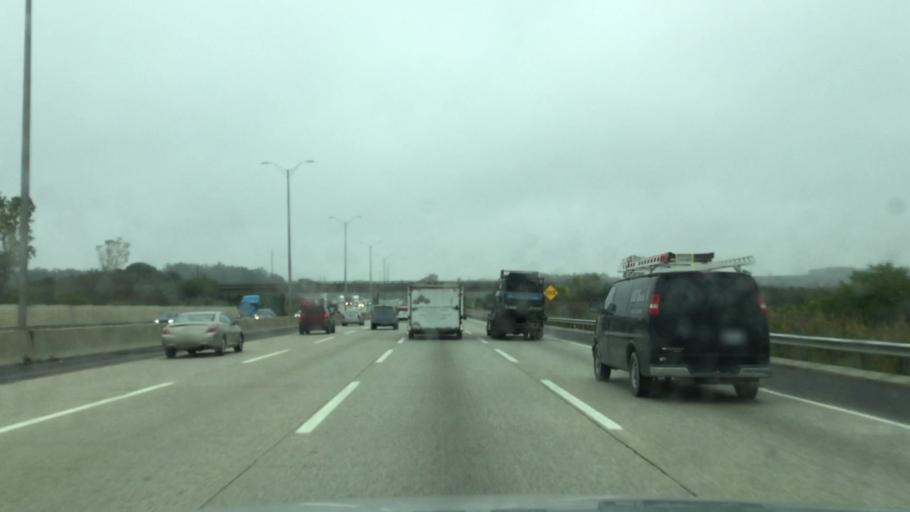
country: US
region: Illinois
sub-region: Lake County
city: Green Oaks
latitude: 42.2892
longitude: -87.9058
